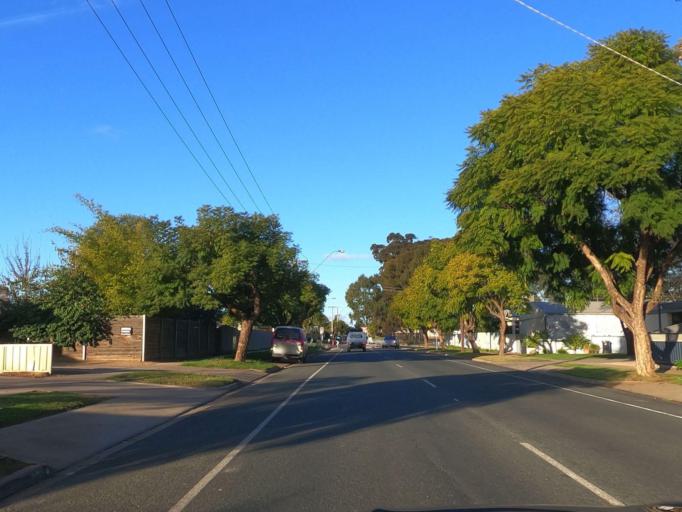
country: AU
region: Victoria
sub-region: Swan Hill
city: Swan Hill
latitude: -35.3475
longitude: 143.5543
